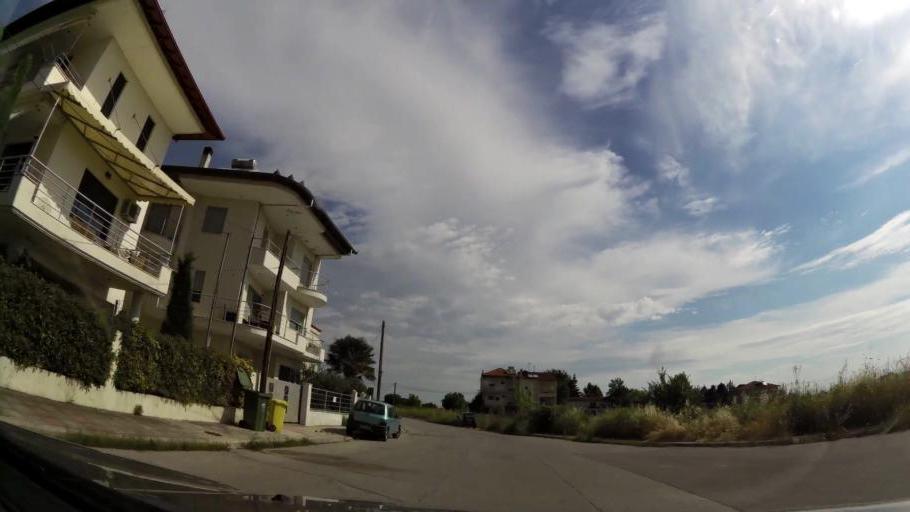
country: GR
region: Central Macedonia
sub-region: Nomos Pierias
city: Katerini
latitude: 40.2852
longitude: 22.5093
